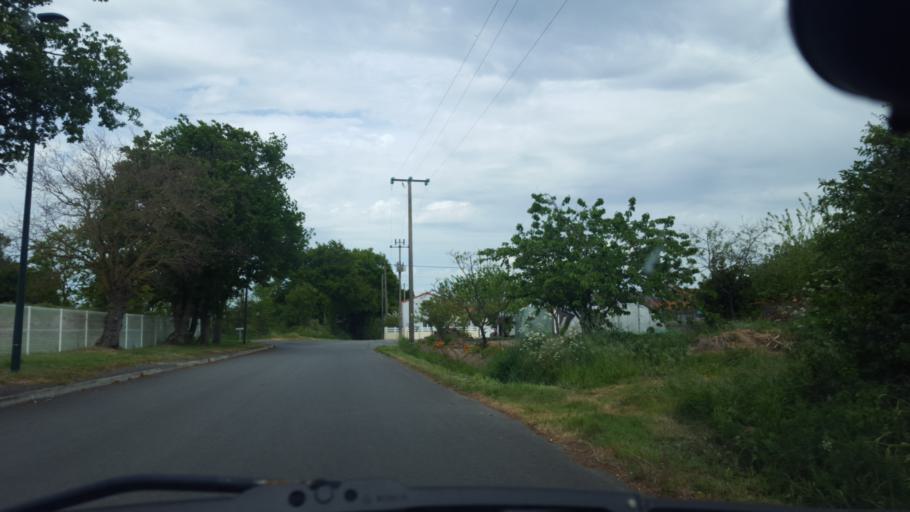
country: FR
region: Pays de la Loire
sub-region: Departement de la Loire-Atlantique
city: Machecoul
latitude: 46.9775
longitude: -1.7980
